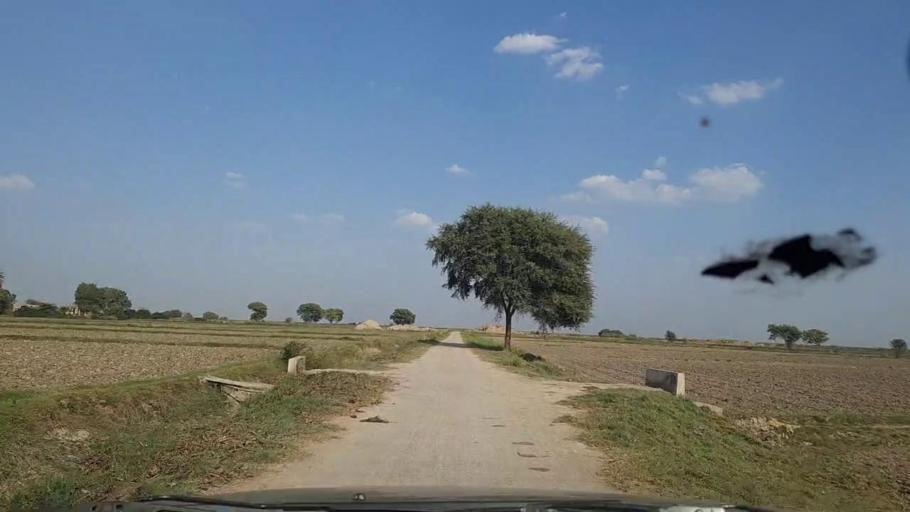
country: PK
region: Sindh
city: Daro Mehar
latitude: 24.8303
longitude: 68.1009
